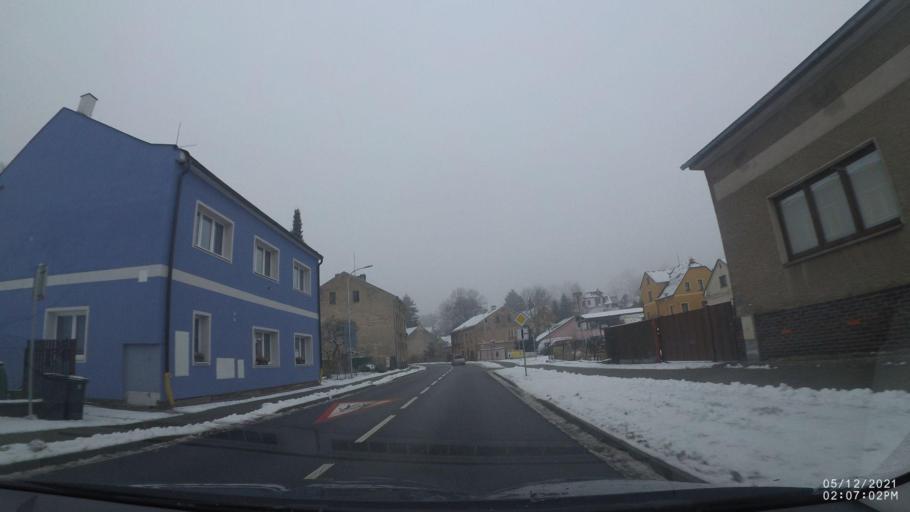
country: CZ
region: Kralovehradecky
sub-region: Okres Nachod
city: Cerveny Kostelec
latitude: 50.4802
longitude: 16.0986
